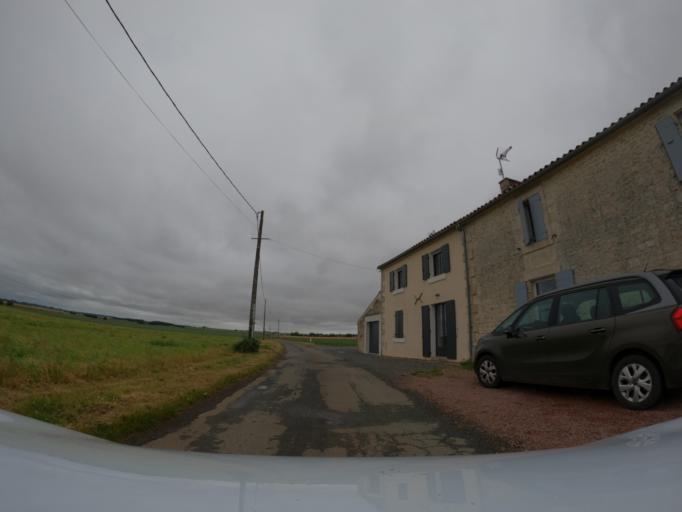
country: FR
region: Pays de la Loire
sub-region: Departement de la Vendee
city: Maillezais
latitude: 46.4188
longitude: -0.7188
